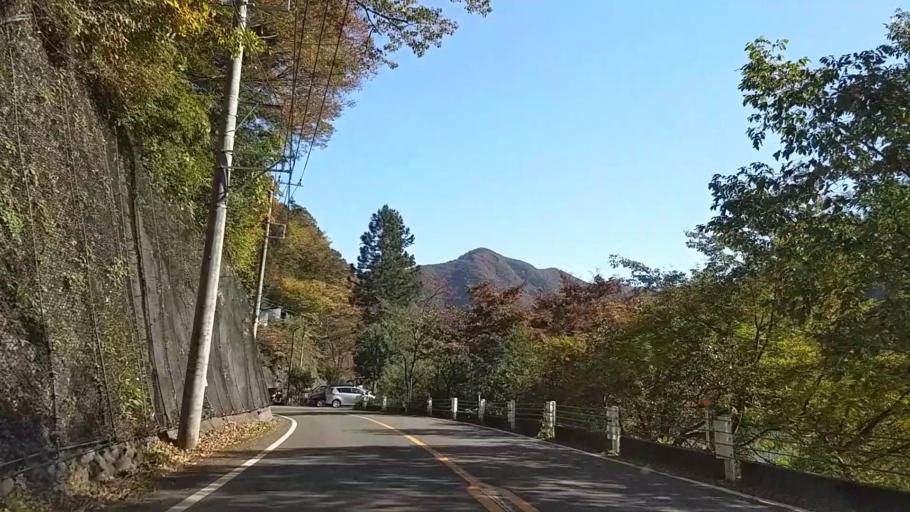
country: JP
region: Yamanashi
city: Uenohara
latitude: 35.7789
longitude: 139.0109
